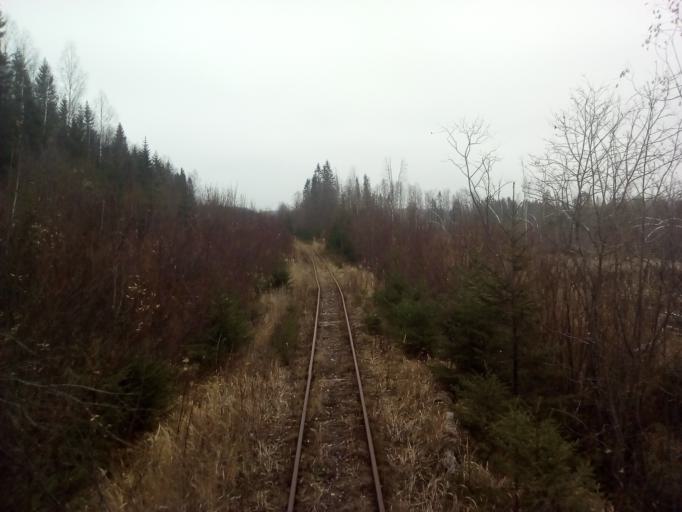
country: RU
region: Vologda
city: Kharovsk
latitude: 59.8031
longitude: 40.4519
